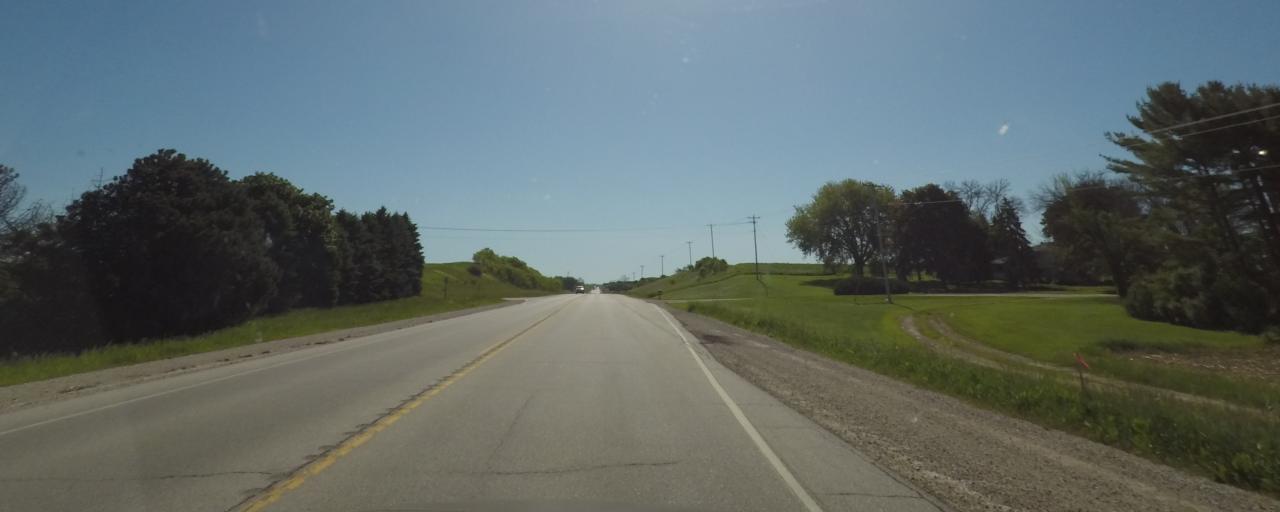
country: US
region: Wisconsin
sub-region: Fond du Lac County
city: Saint Peter
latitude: 43.7834
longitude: -88.3426
